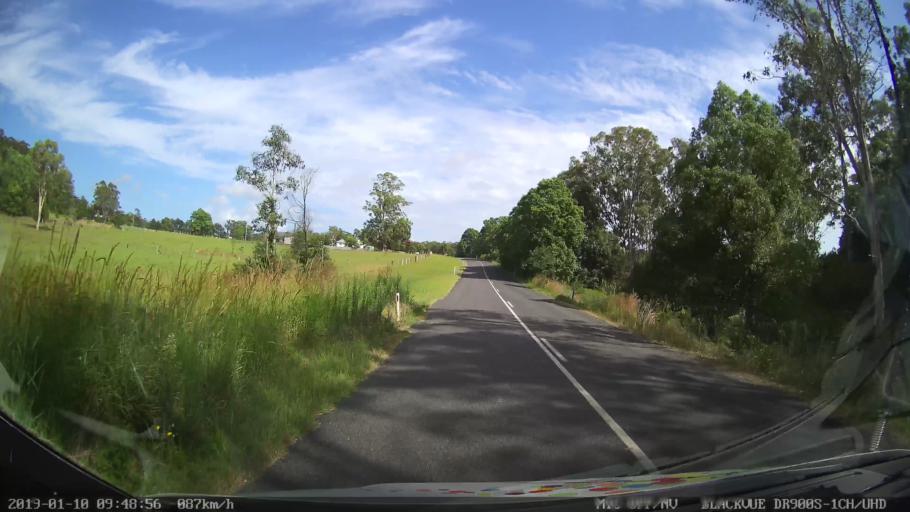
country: AU
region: New South Wales
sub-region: Coffs Harbour
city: Nana Glen
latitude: -30.0669
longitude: 152.9838
